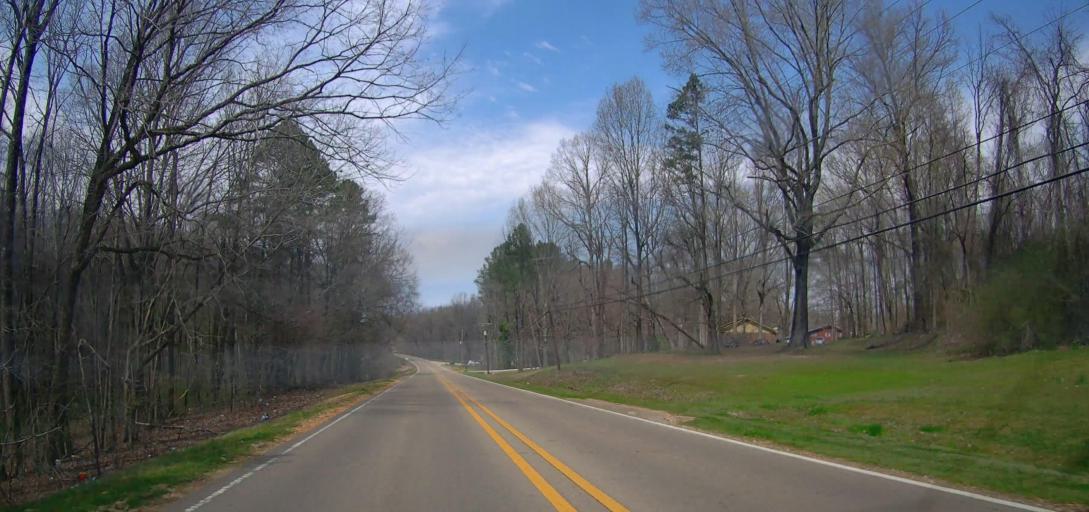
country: US
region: Mississippi
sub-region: Union County
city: New Albany
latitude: 34.4629
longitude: -88.9806
